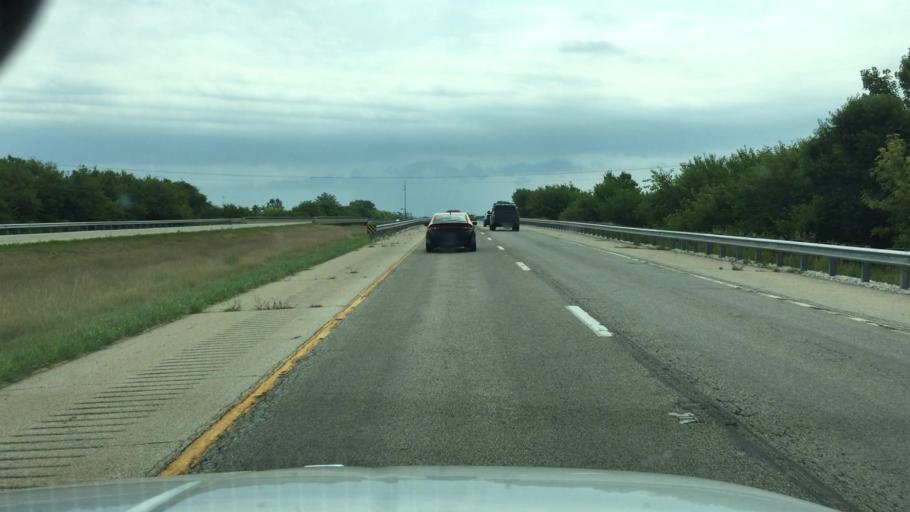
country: US
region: Illinois
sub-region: Peoria County
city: Elmwood
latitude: 40.8357
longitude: -89.8917
